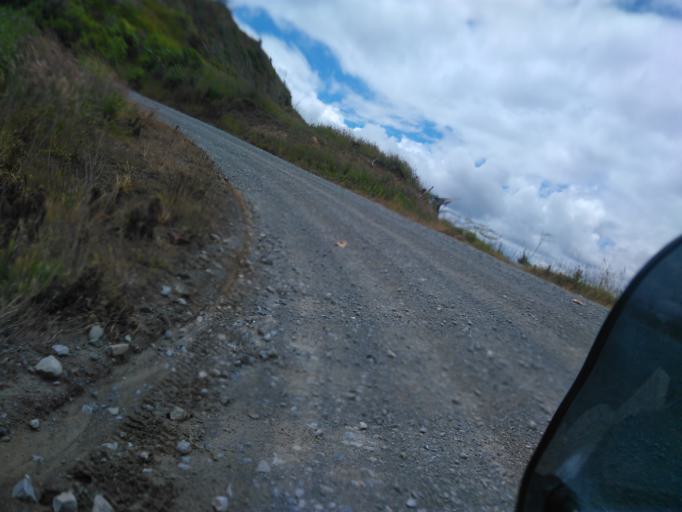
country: NZ
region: Gisborne
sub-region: Gisborne District
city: Gisborne
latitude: -38.1793
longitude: 178.1280
